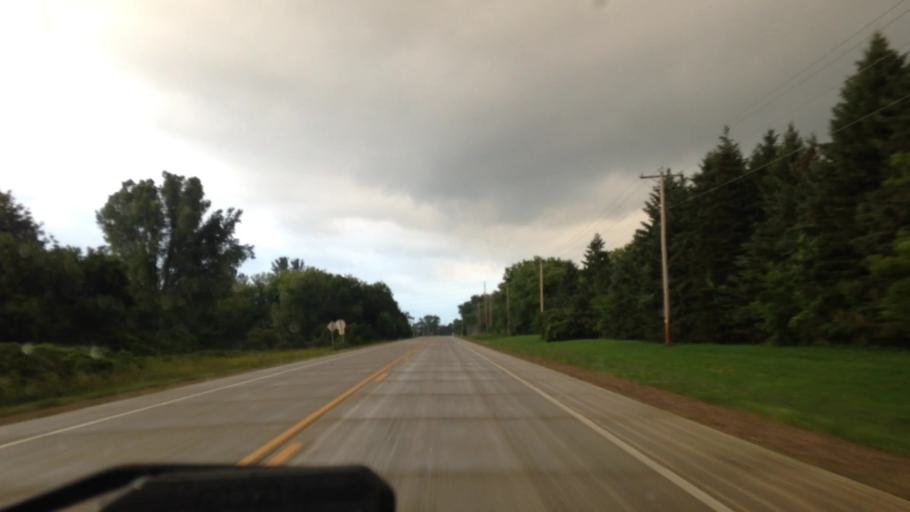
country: US
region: Wisconsin
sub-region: Dodge County
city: Mayville
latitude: 43.4763
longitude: -88.5554
